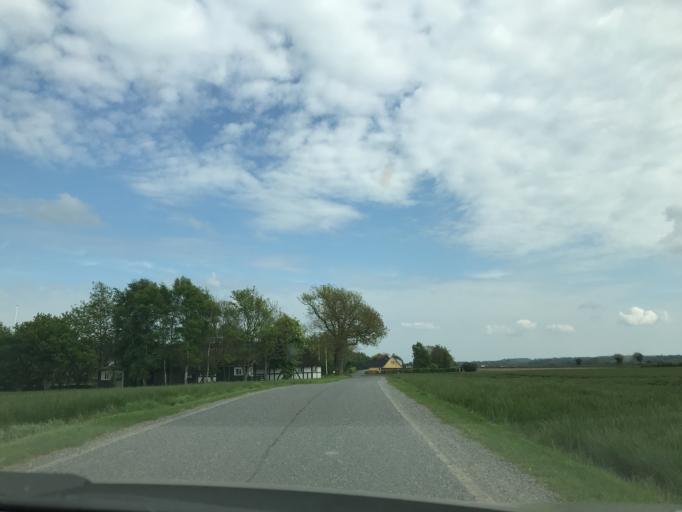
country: DK
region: South Denmark
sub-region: Assens Kommune
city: Assens
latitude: 55.3304
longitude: 9.8971
